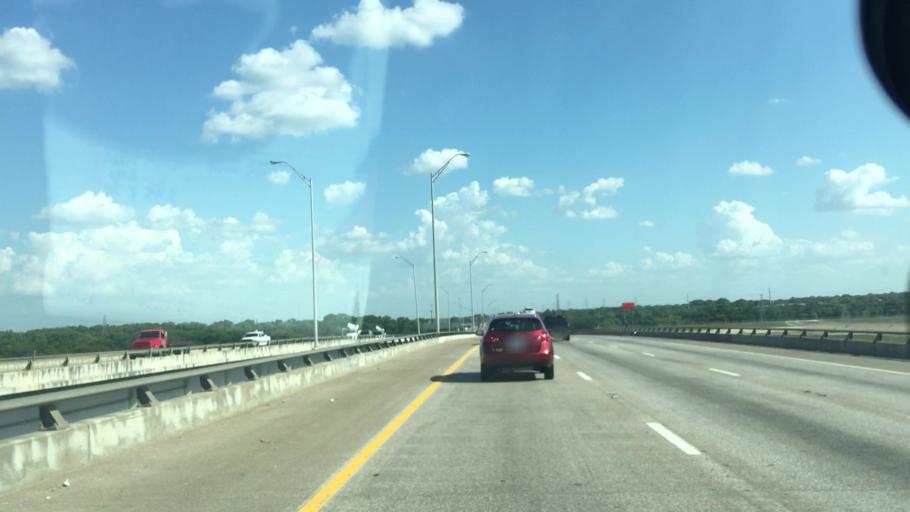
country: US
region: Texas
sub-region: Dallas County
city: Dallas
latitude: 32.7365
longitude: -96.7660
